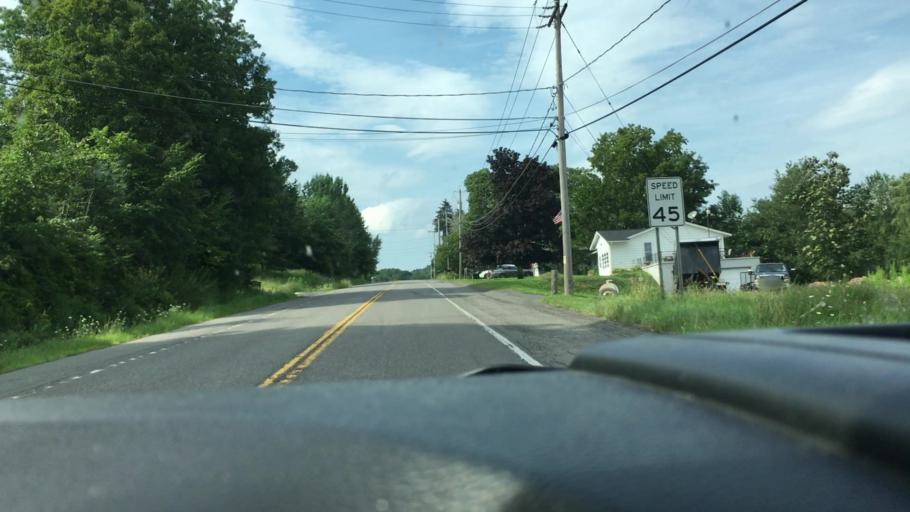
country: US
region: New York
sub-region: Onondaga County
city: Nedrow
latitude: 42.8851
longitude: -76.0940
